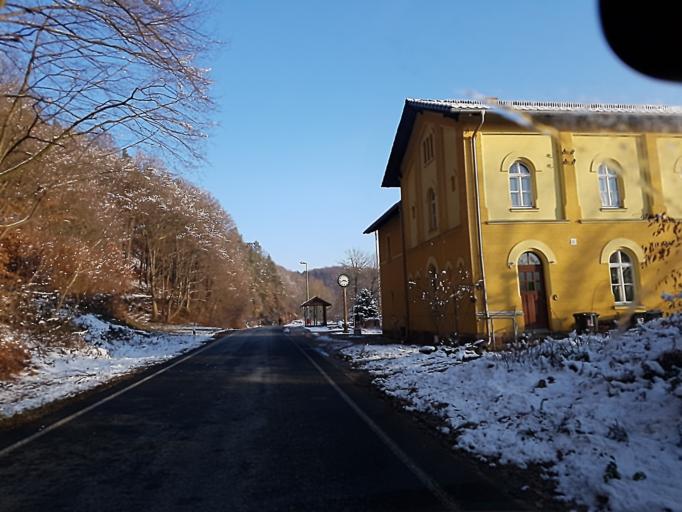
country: DE
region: Saxony
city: Grossweitzschen
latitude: 51.1580
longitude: 13.0034
